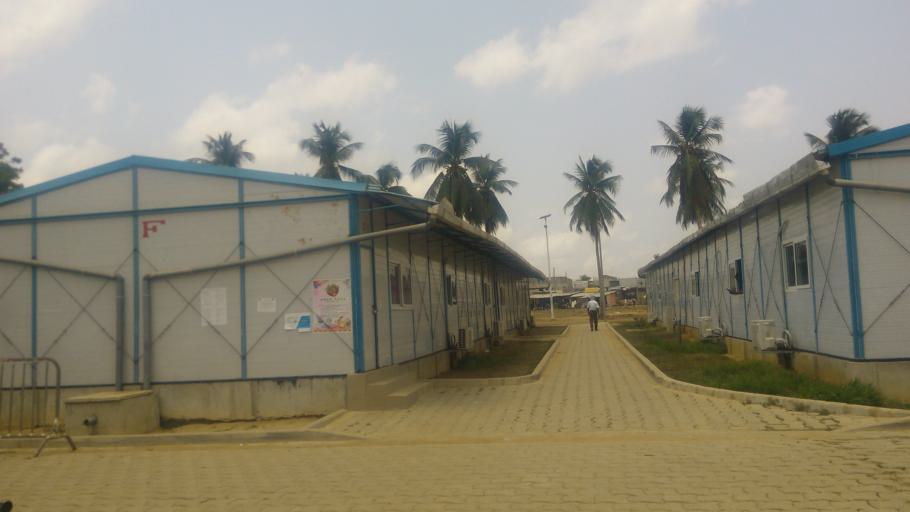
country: BJ
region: Atlantique
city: Abomey-Calavi
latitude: 6.4214
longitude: 2.3404
